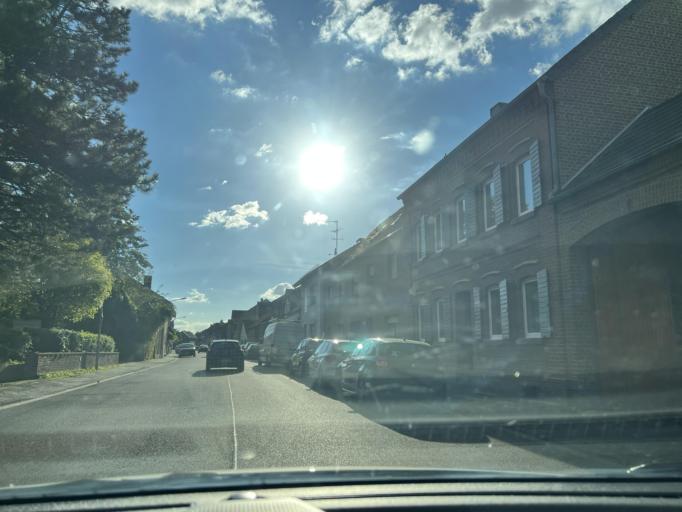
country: DE
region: North Rhine-Westphalia
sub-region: Regierungsbezirk Koln
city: Pulheim
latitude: 50.9931
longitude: 6.7396
